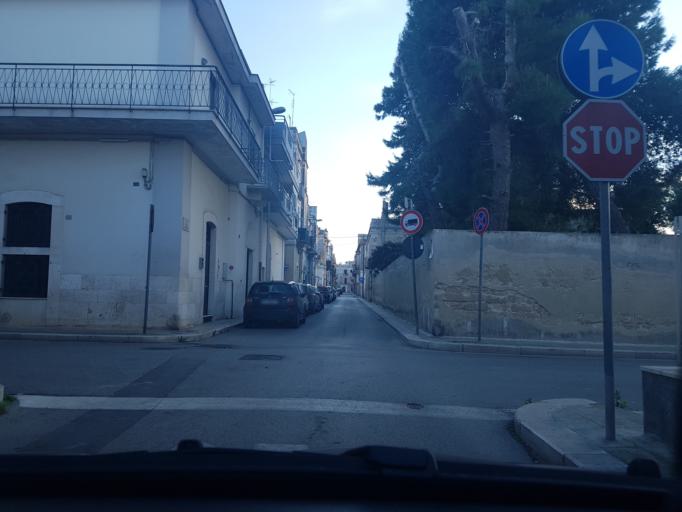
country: IT
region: Apulia
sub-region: Provincia di Bari
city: Bitritto
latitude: 41.0434
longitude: 16.8253
